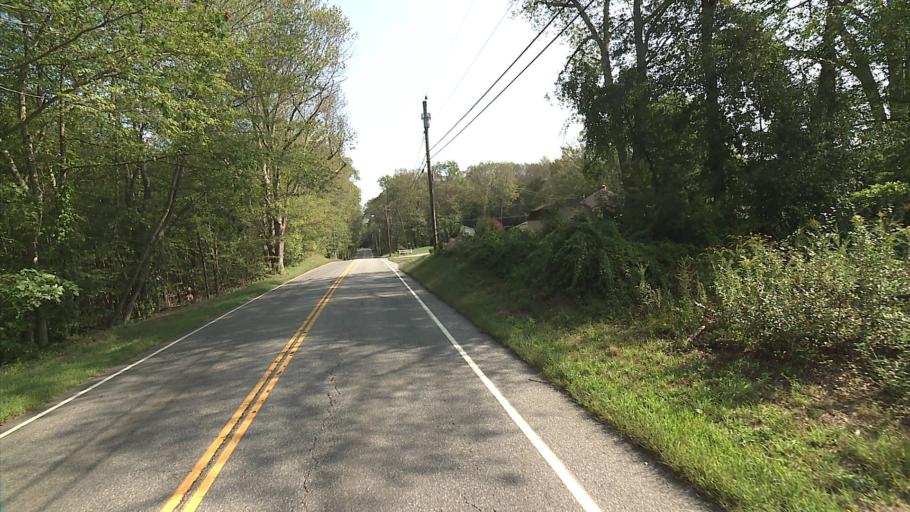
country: US
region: Connecticut
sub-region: New London County
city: Lisbon
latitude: 41.6327
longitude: -71.9991
